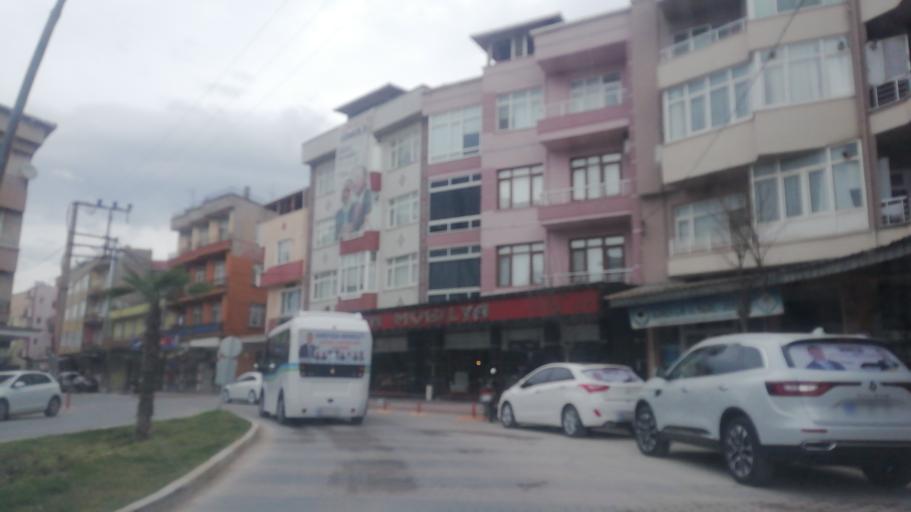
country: TR
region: Balikesir
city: Gonen
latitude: 40.1023
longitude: 27.6522
